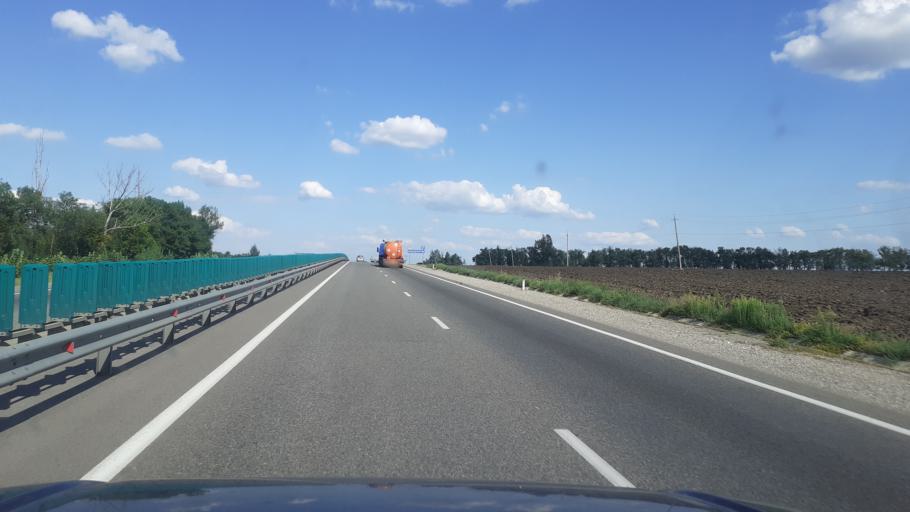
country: RU
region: Krasnodarskiy
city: Severskaya
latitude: 44.8545
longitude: 38.7142
